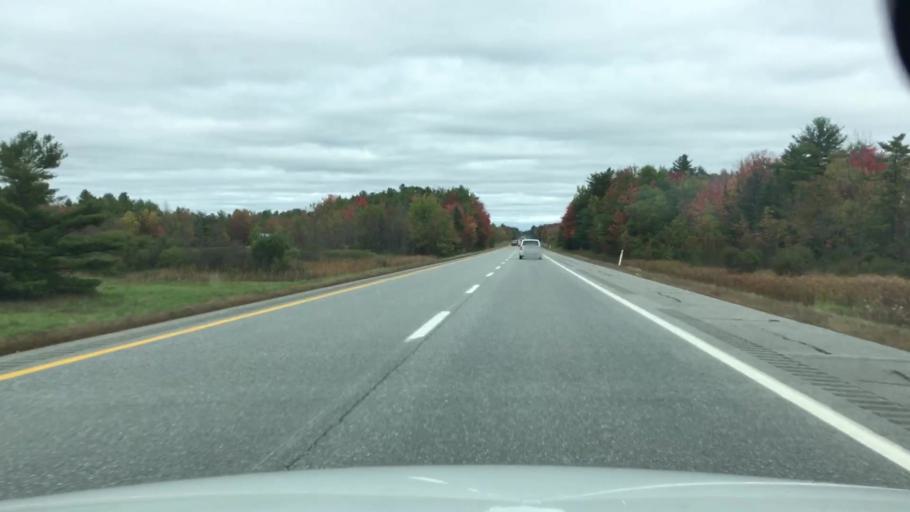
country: US
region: Maine
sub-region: Kennebec County
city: Benton
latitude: 44.6079
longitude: -69.5720
